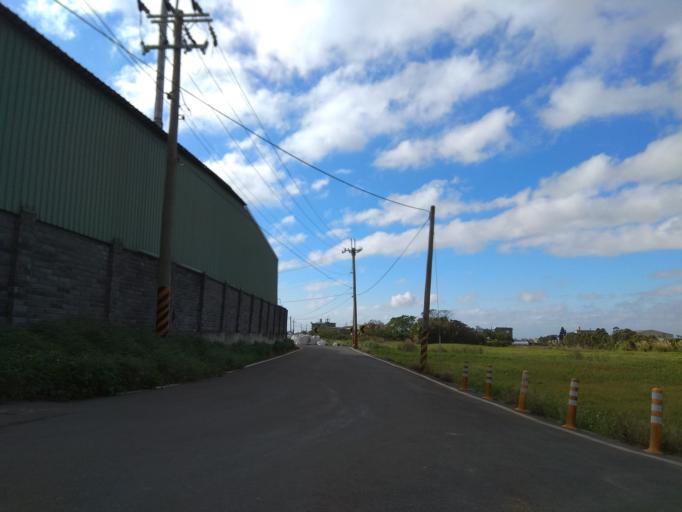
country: TW
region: Taiwan
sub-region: Hsinchu
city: Zhubei
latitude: 24.9720
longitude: 121.0745
